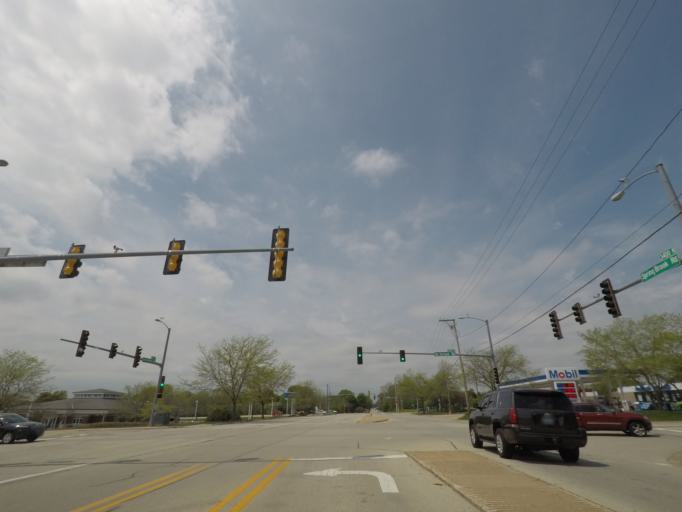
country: US
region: Illinois
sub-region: Winnebago County
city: Machesney Park
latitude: 42.3080
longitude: -88.9775
